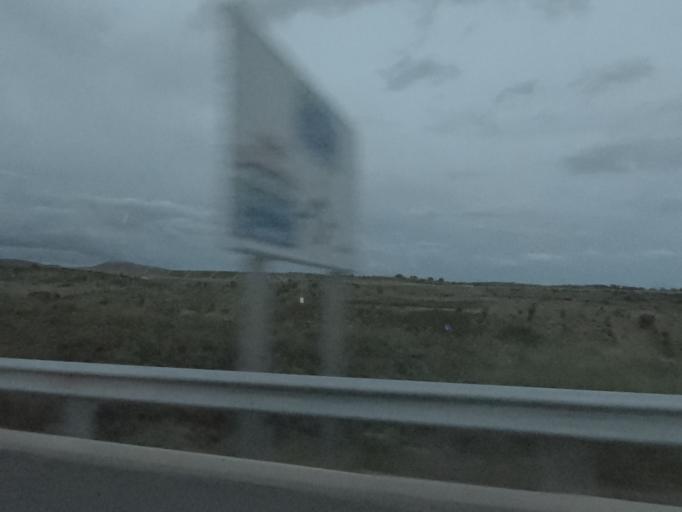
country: ES
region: Extremadura
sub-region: Provincia de Caceres
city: Canaveral
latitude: 39.7973
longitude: -6.3674
